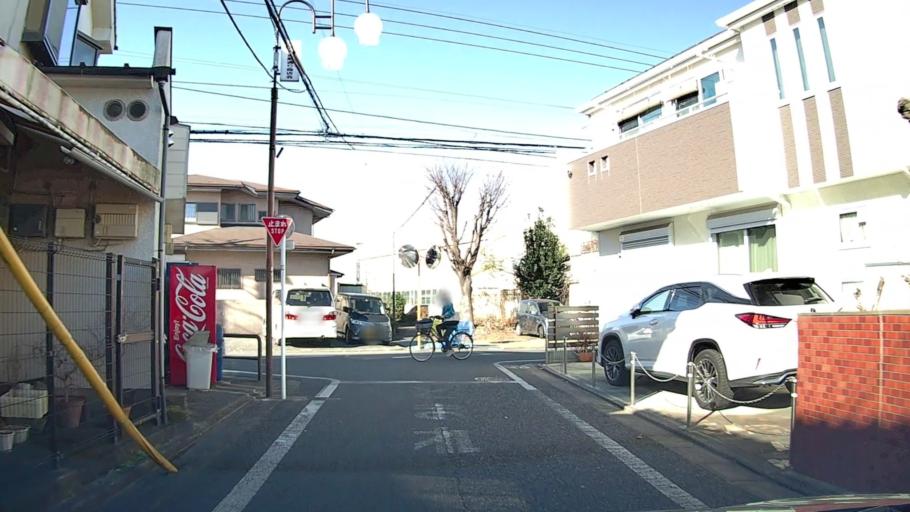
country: JP
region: Saitama
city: Wako
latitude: 35.7589
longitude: 139.6119
